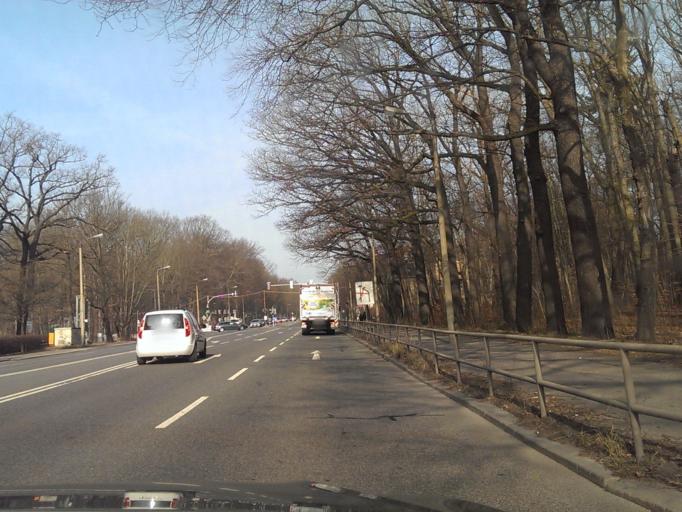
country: DE
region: Saxony
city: Chemnitz
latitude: 50.8477
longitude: 12.8993
